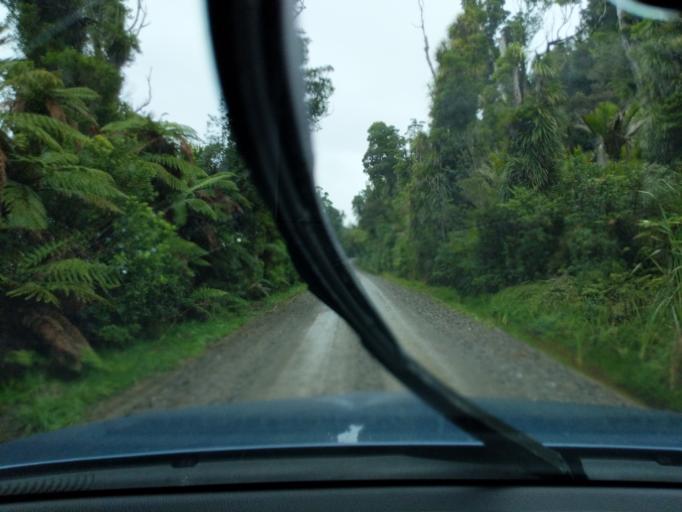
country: NZ
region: Tasman
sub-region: Tasman District
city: Takaka
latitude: -40.6442
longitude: 172.4785
